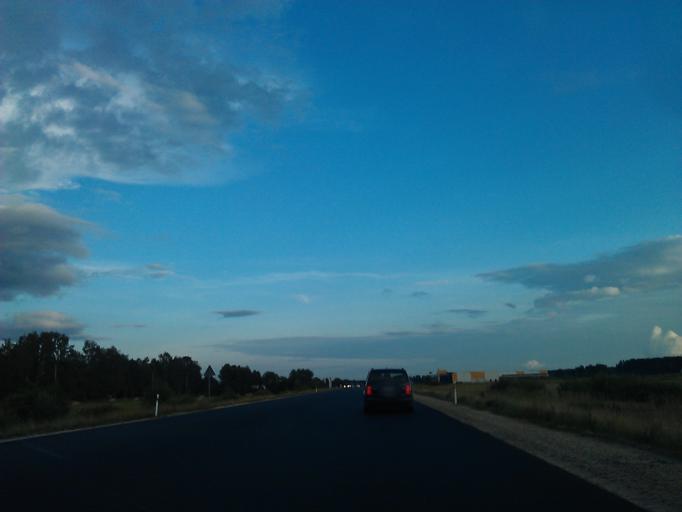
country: LV
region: Adazi
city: Adazi
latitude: 57.0937
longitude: 24.3120
